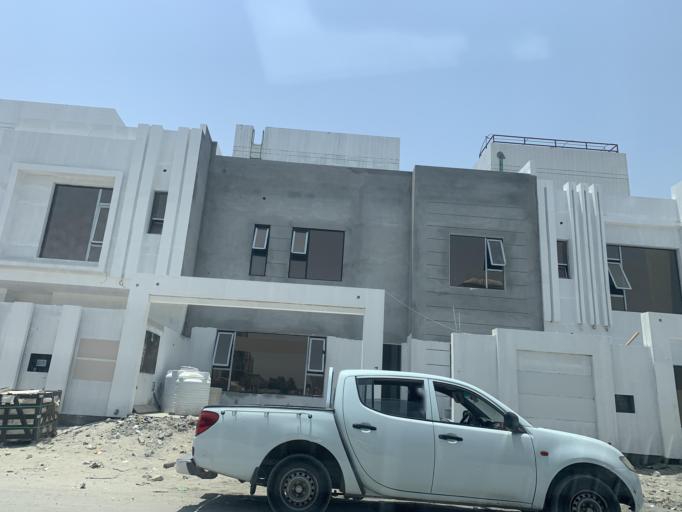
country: BH
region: Manama
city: Jidd Hafs
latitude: 26.2119
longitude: 50.4682
